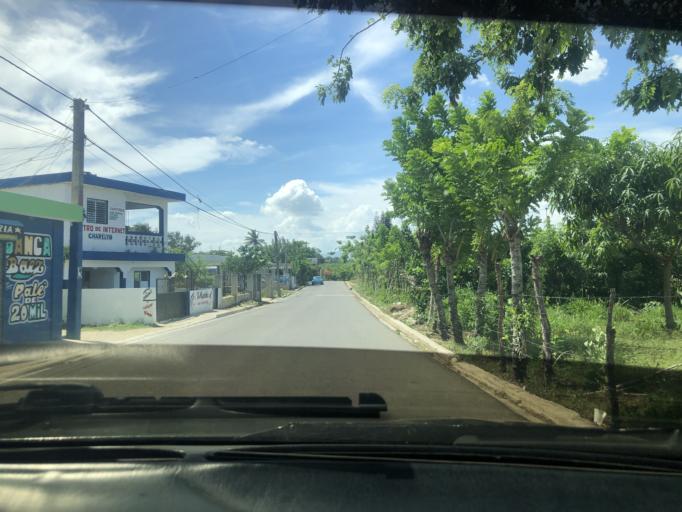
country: DO
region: Santiago
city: Santiago de los Caballeros
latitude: 19.3990
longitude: -70.6641
